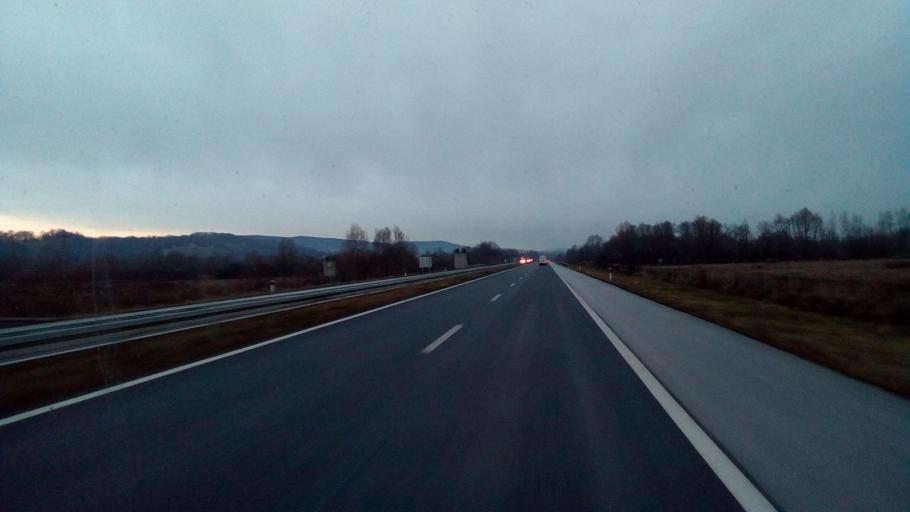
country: HR
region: Zagrebacka
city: Brckovljani
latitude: 45.9264
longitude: 16.2720
